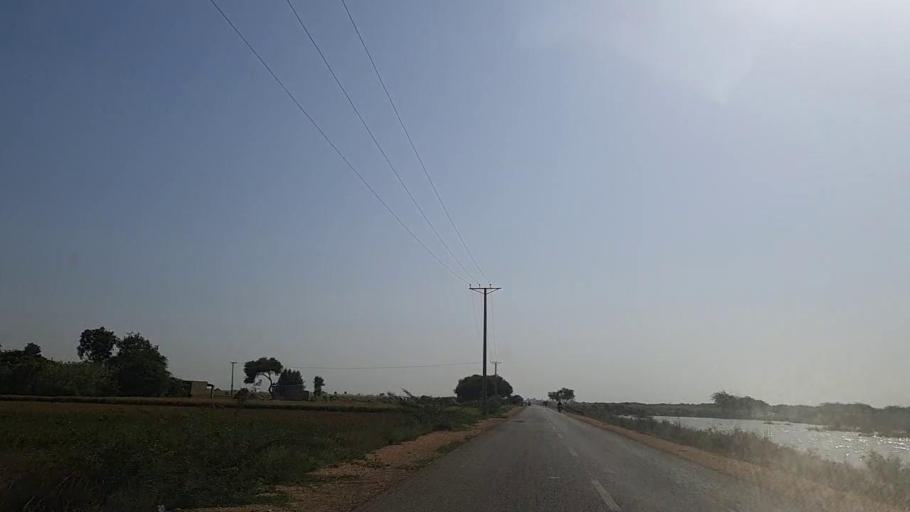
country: PK
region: Sindh
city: Jati
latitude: 24.5404
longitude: 68.2798
